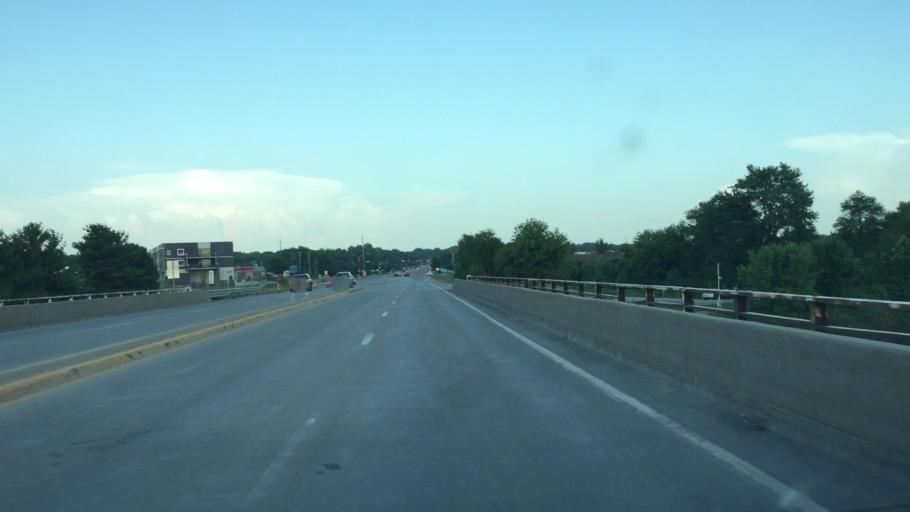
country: US
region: Iowa
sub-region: Johnson County
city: Iowa City
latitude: 41.6466
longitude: -91.5366
